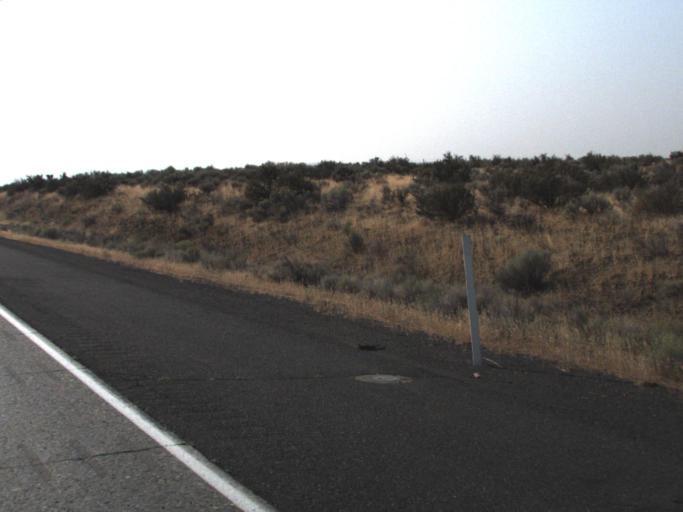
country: US
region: Washington
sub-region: Kittitas County
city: Kittitas
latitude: 46.8178
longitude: -120.3570
